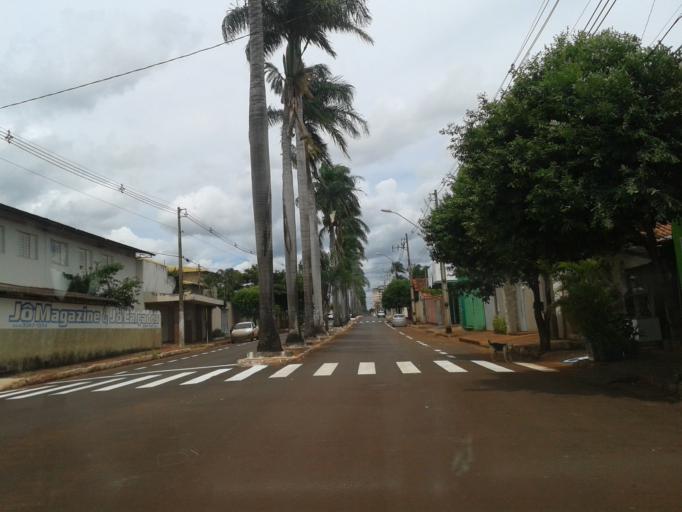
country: BR
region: Minas Gerais
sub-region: Centralina
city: Centralina
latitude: -18.5819
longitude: -49.1987
